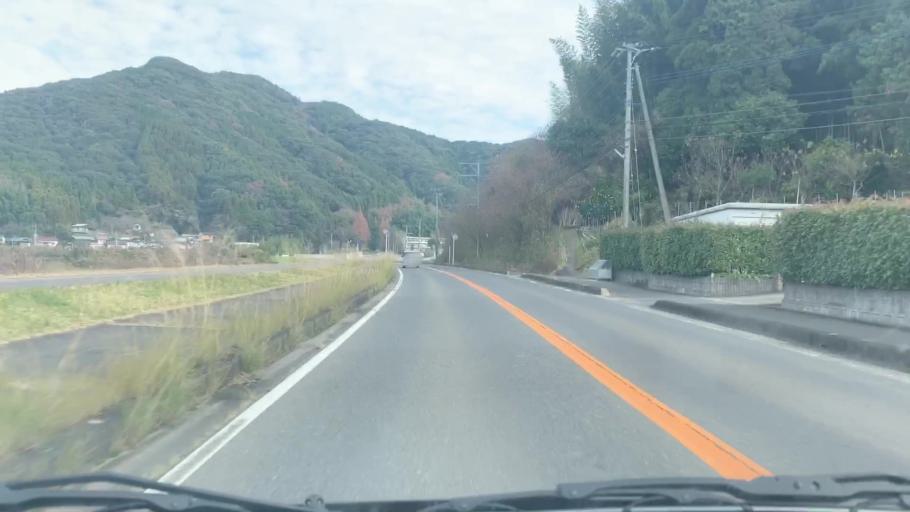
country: JP
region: Saga Prefecture
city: Karatsu
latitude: 33.3598
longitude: 130.0084
